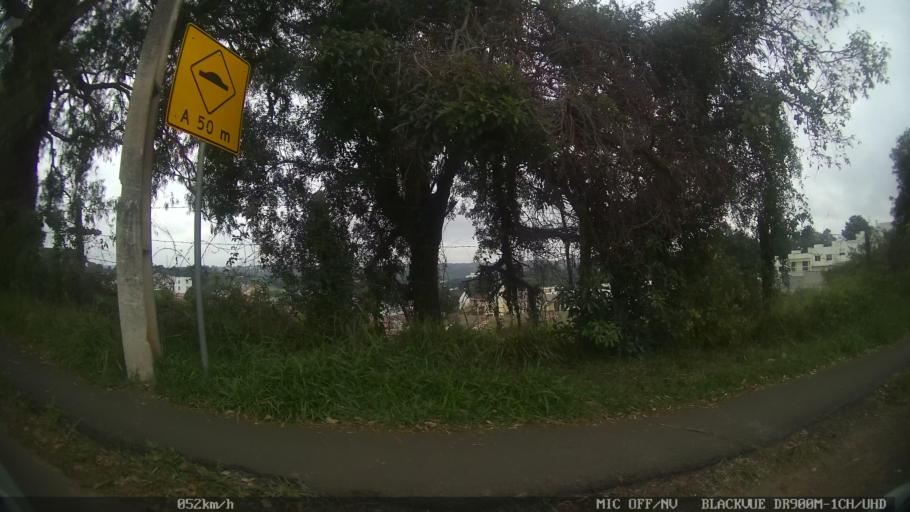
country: BR
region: Parana
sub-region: Almirante Tamandare
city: Almirante Tamandare
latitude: -25.3652
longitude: -49.2719
